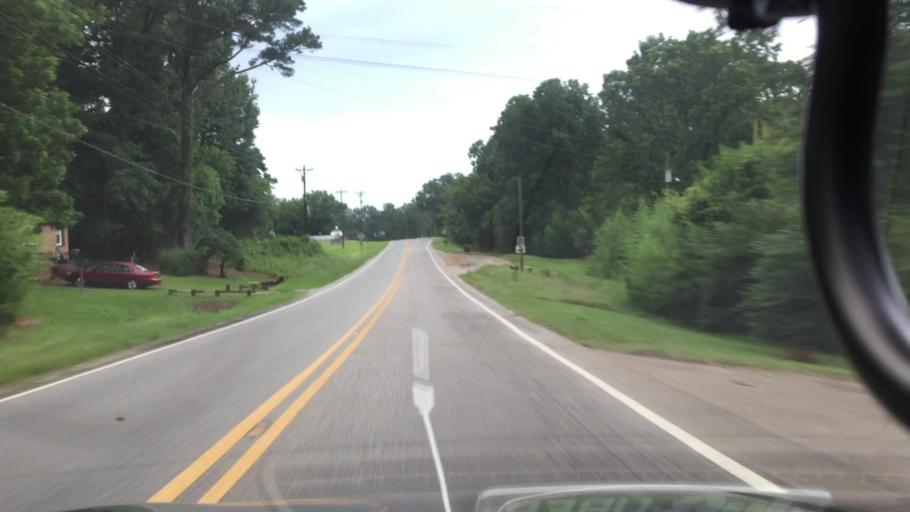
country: US
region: Alabama
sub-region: Pike County
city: Troy
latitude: 31.6934
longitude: -85.9599
